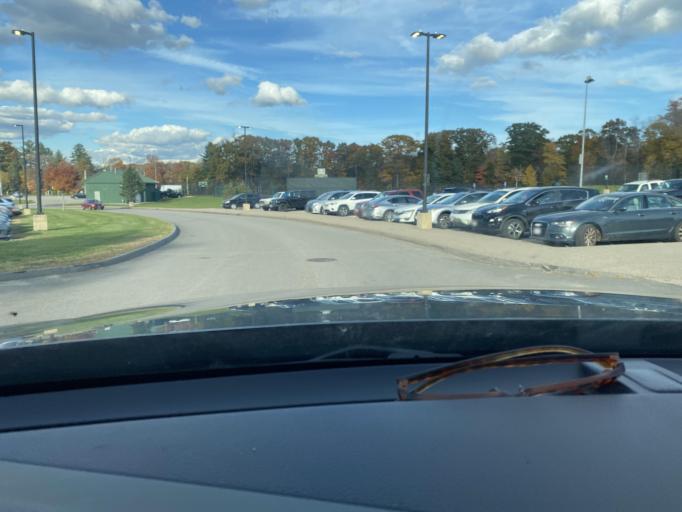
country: US
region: Massachusetts
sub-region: Norfolk County
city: Westwood
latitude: 42.2163
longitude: -71.2154
